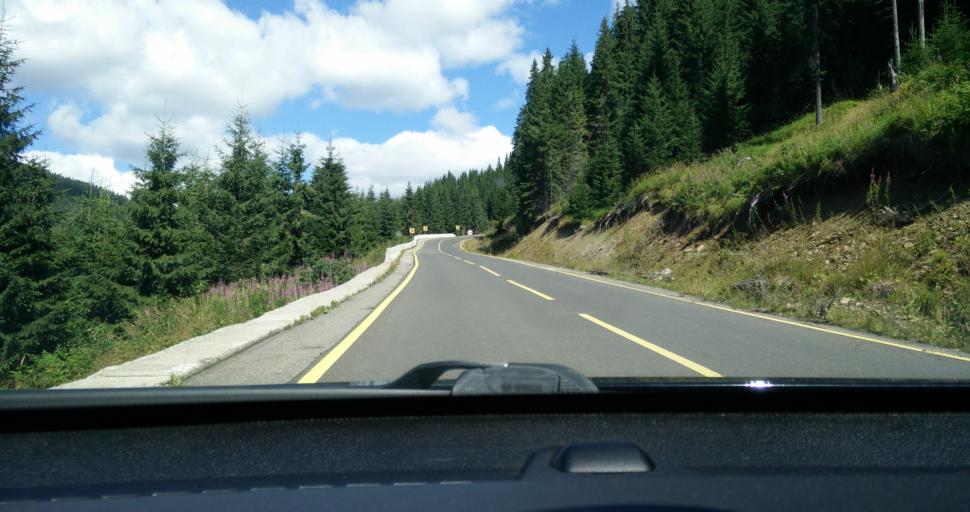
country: RO
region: Hunedoara
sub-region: Oras Petrila
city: Petrila
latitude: 45.4476
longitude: 23.6209
